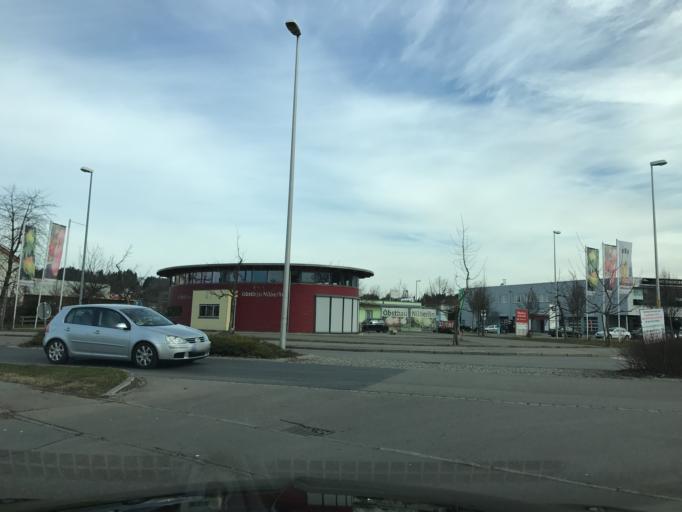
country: AT
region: Vorarlberg
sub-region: Politischer Bezirk Bregenz
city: Horbranz
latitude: 47.5484
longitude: 9.7280
